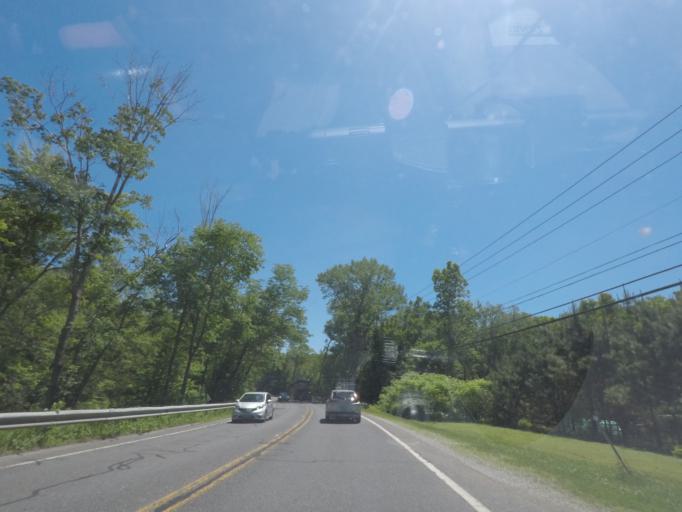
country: US
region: Massachusetts
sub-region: Berkshire County
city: Becket
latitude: 42.2704
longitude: -73.1407
